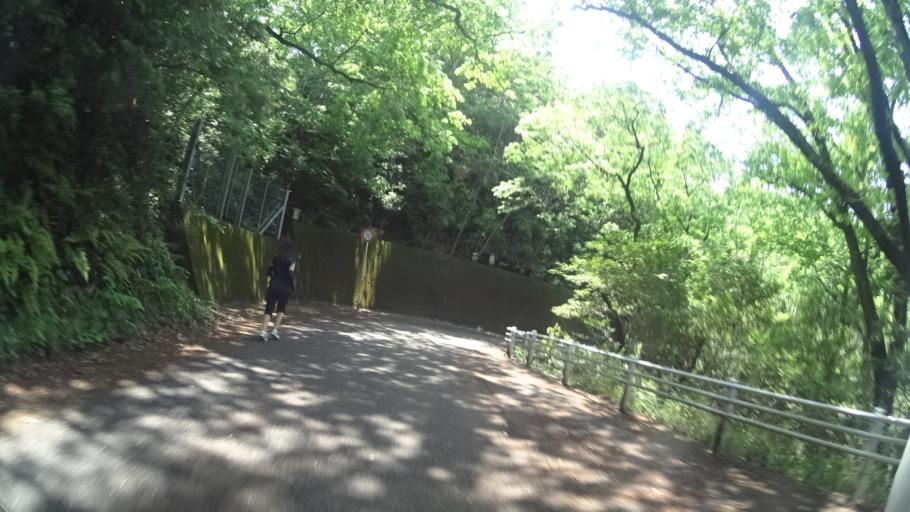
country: JP
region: Tokushima
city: Tokushima-shi
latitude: 34.0674
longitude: 134.5180
